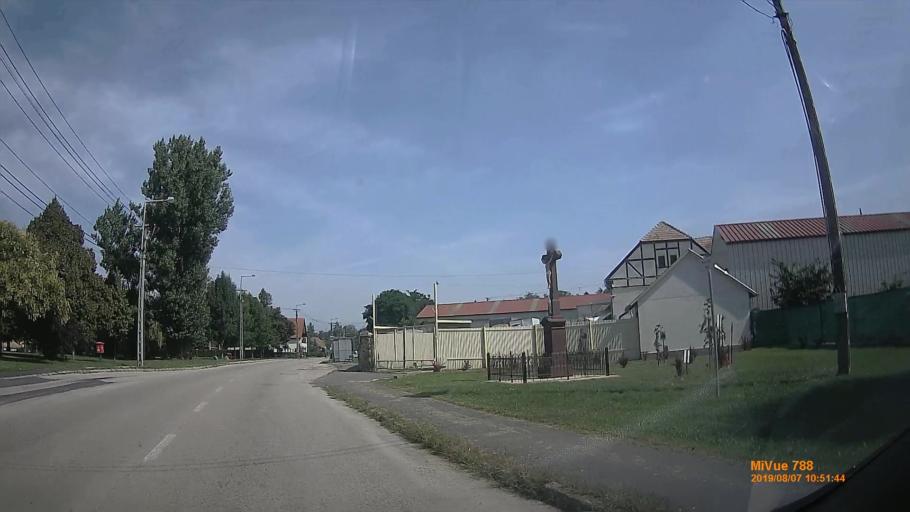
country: HU
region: Veszprem
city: Ajka
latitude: 47.0894
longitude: 17.5640
